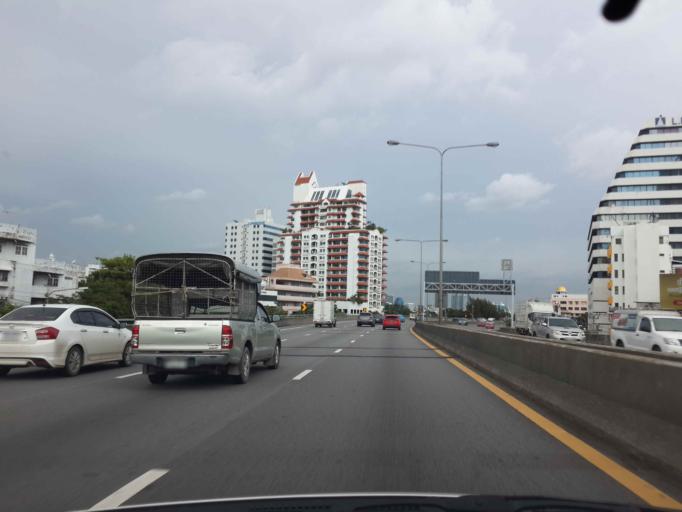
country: TH
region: Bangkok
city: Yan Nawa
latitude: 13.7030
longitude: 100.5430
